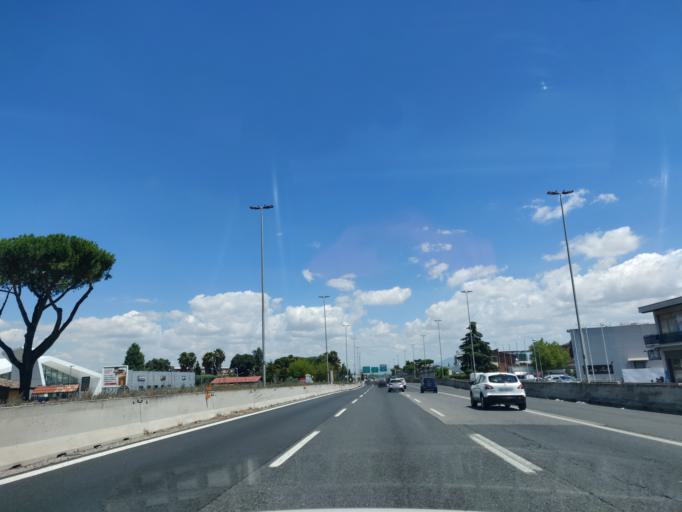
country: IT
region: Latium
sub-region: Citta metropolitana di Roma Capitale
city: Ciampino
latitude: 41.8258
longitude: 12.5826
